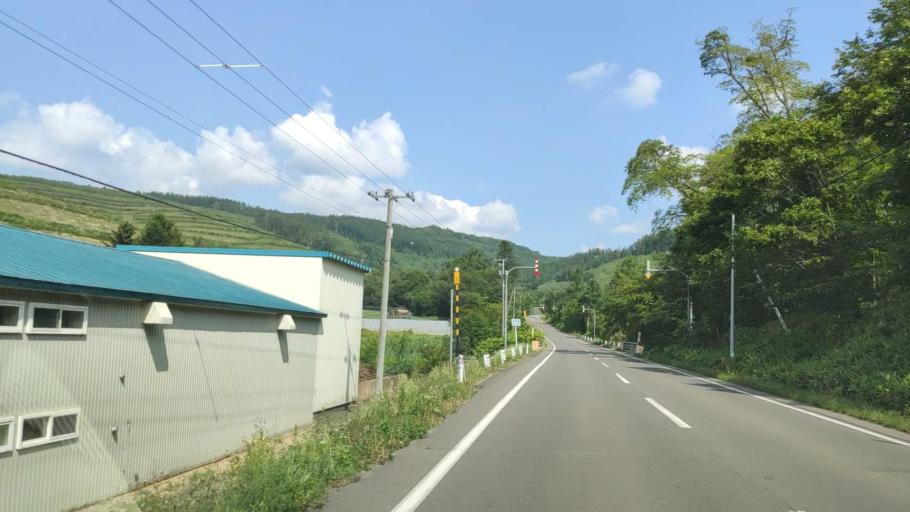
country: JP
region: Hokkaido
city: Shimo-furano
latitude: 43.4221
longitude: 142.4012
